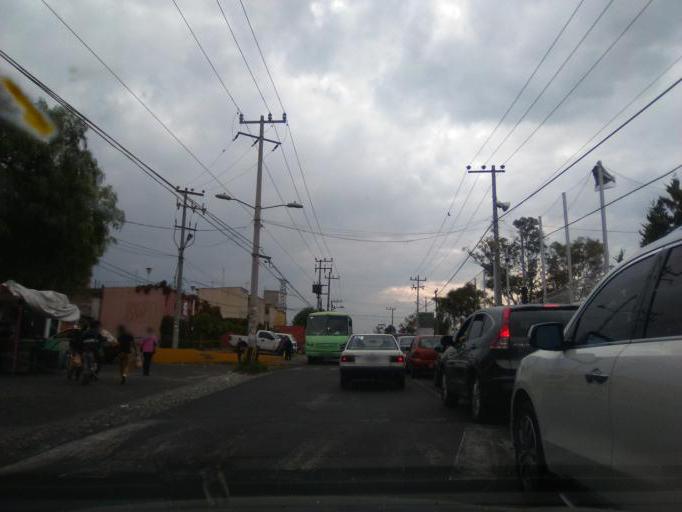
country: MX
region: Mexico City
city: Col. Bosques de las Lomas
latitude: 19.3654
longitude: -99.2438
